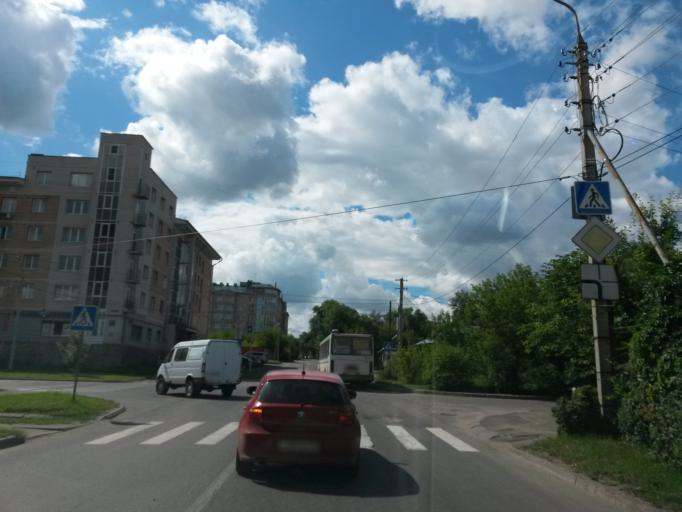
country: RU
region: Jaroslavl
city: Yaroslavl
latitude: 57.6065
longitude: 39.8723
